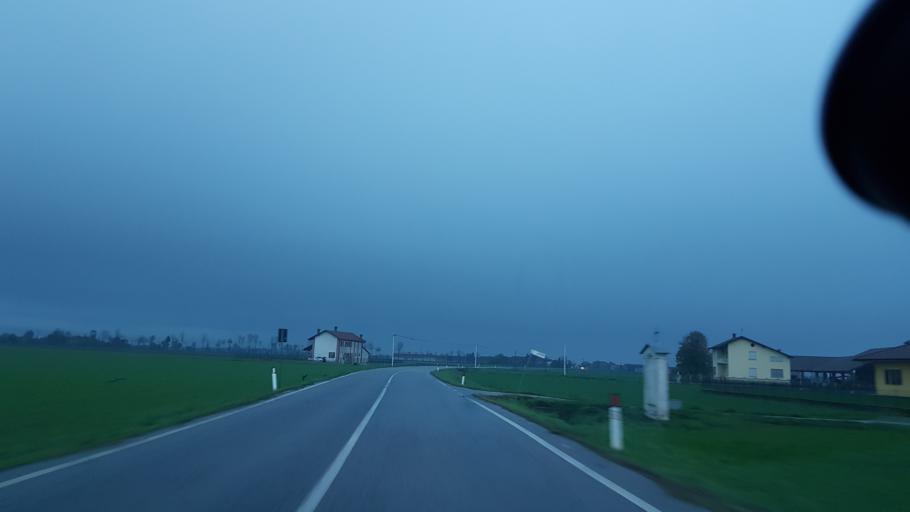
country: IT
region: Piedmont
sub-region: Provincia di Cuneo
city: Fossano
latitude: 44.5580
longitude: 7.6857
